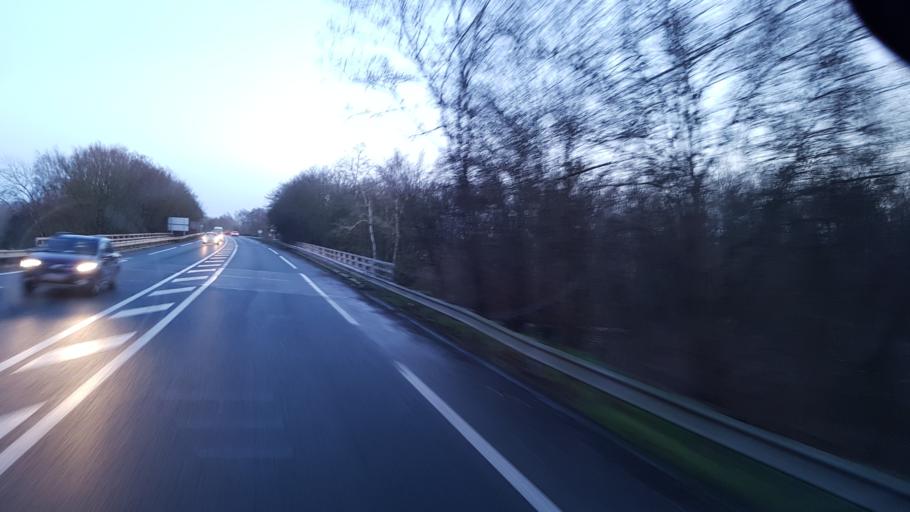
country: FR
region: Nord-Pas-de-Calais
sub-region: Departement du Nord
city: Courchelettes
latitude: 50.3569
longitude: 3.0472
